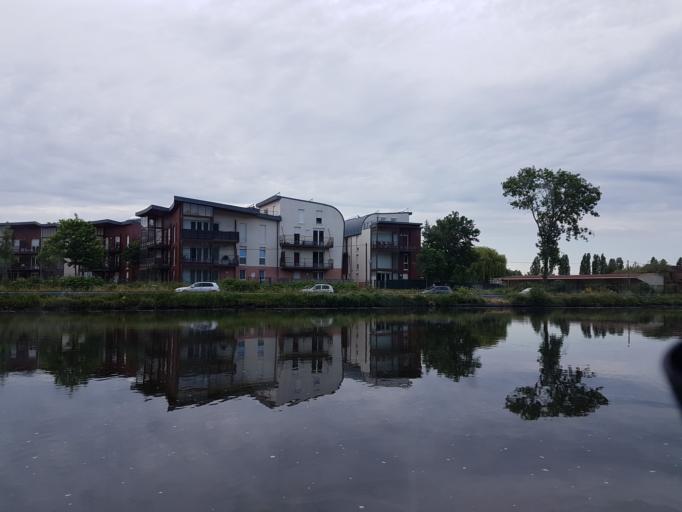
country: FR
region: Bourgogne
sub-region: Departement de l'Yonne
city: Auxerre
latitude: 47.8114
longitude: 3.5783
